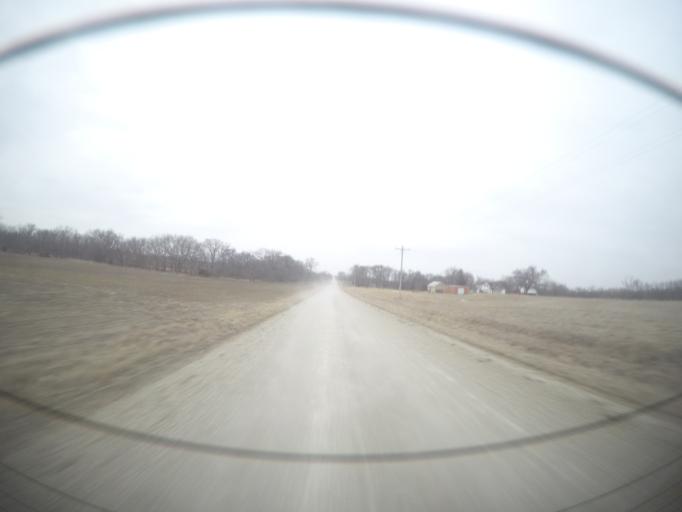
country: US
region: Kansas
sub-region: Pottawatomie County
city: Wamego
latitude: 39.1486
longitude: -96.2407
